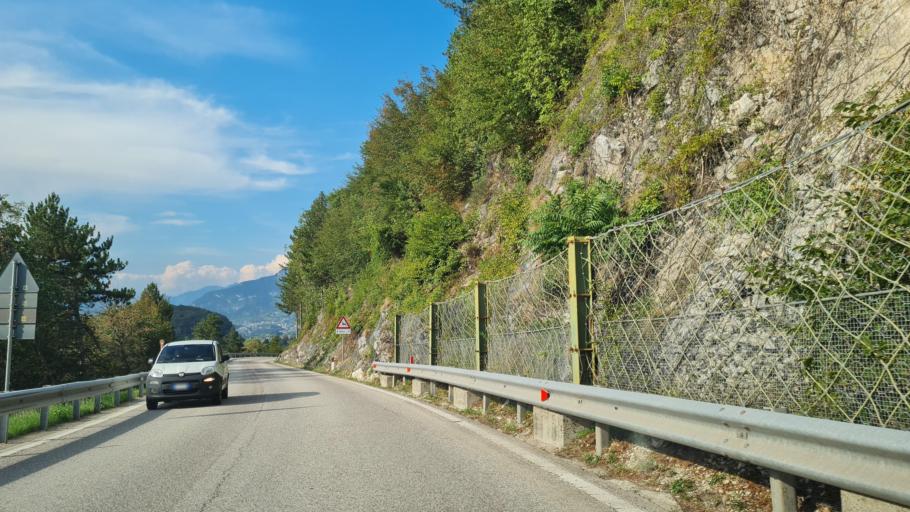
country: IT
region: Trentino-Alto Adige
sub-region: Provincia di Trento
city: Mattarello
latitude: 46.0183
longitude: 11.1451
